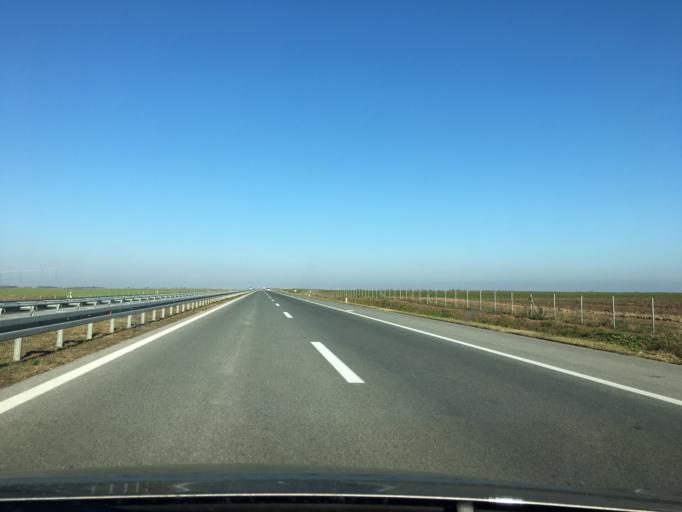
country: RS
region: Autonomna Pokrajina Vojvodina
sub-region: Severnobacki Okrug
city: Mali Igos
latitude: 45.7090
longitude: 19.7159
